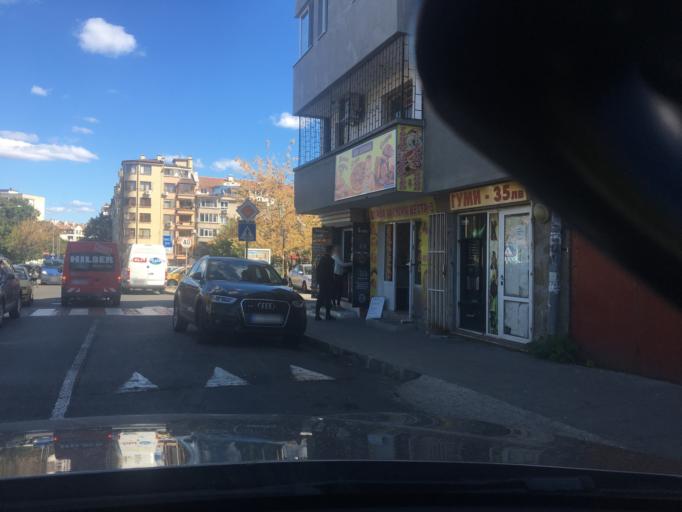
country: BG
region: Burgas
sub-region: Obshtina Burgas
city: Burgas
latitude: 42.5081
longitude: 27.4722
